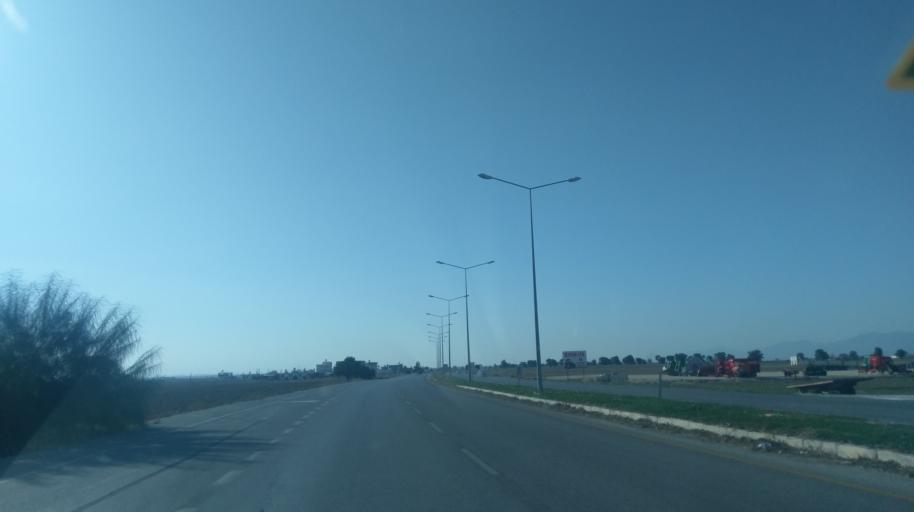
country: CY
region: Ammochostos
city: Acheritou
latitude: 35.1714
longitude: 33.7882
